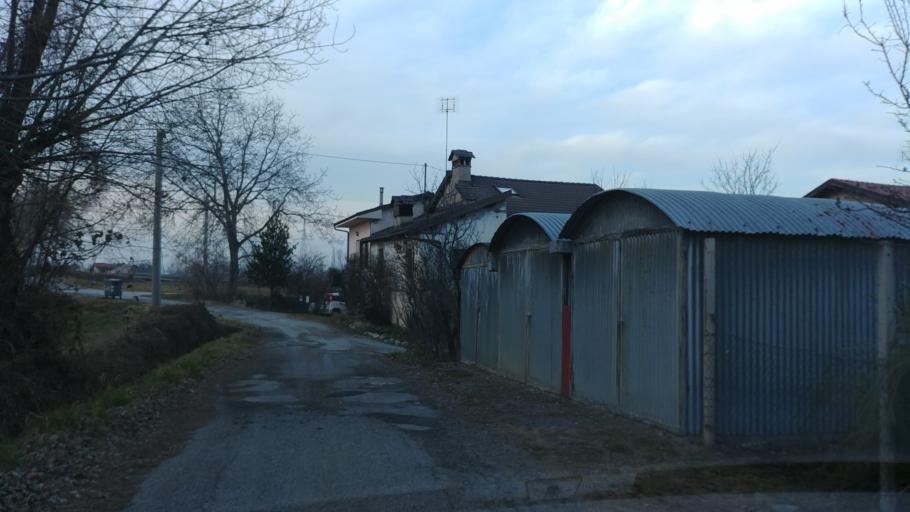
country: IT
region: Piedmont
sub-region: Provincia di Cuneo
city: Cuneo
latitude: 44.3954
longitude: 7.5279
